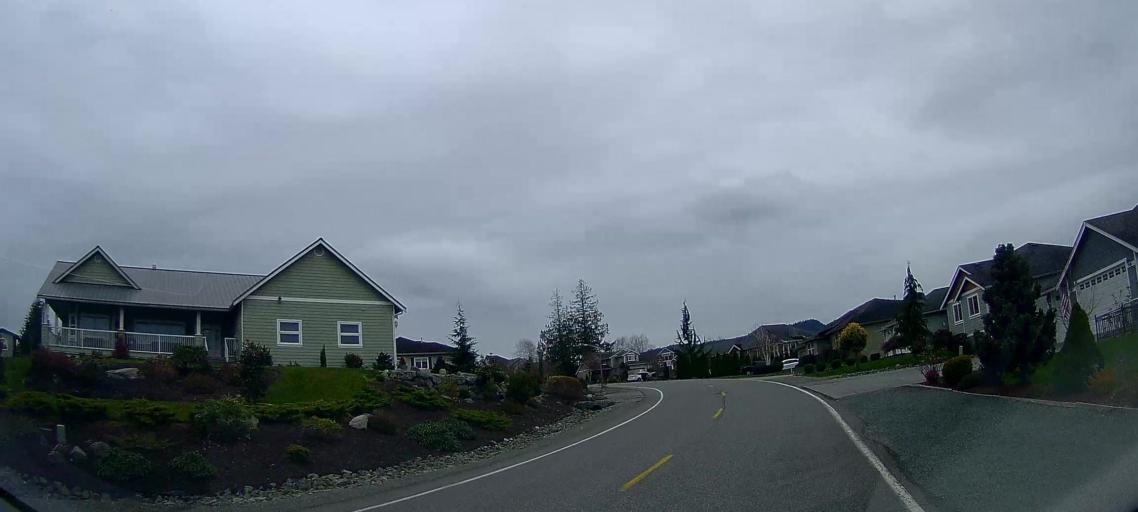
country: US
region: Washington
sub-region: Skagit County
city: Big Lake
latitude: 48.4000
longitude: -122.2305
